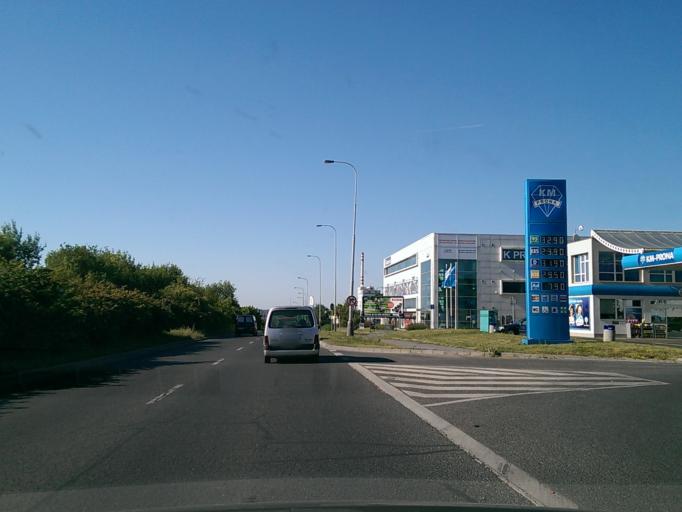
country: CZ
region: Praha
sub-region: Praha 14
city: Hostavice
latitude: 50.0635
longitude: 14.5374
